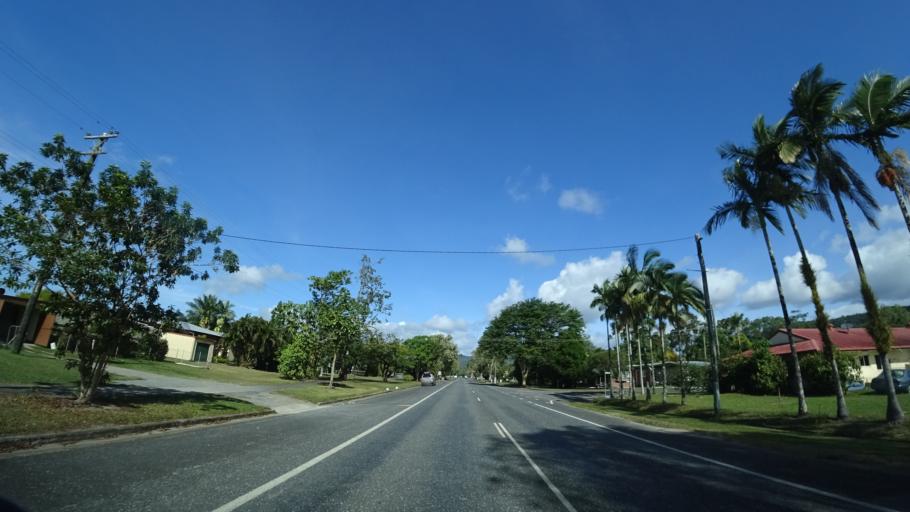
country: AU
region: Queensland
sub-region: Cairns
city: Port Douglas
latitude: -16.4731
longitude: 145.3742
